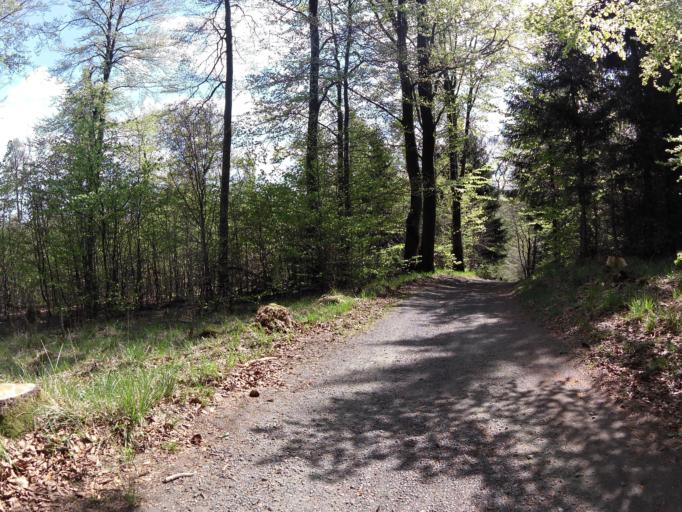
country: DE
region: Thuringia
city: Finsterbergen
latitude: 50.7965
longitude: 10.5404
